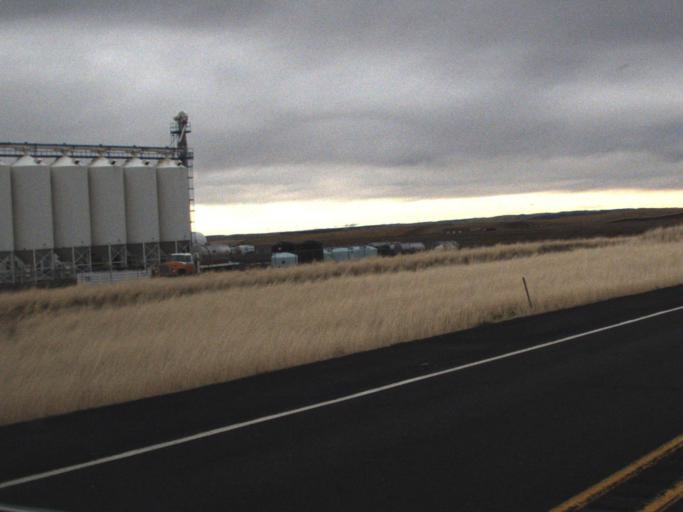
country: US
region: Washington
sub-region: Walla Walla County
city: Walla Walla East
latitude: 46.0930
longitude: -118.2565
